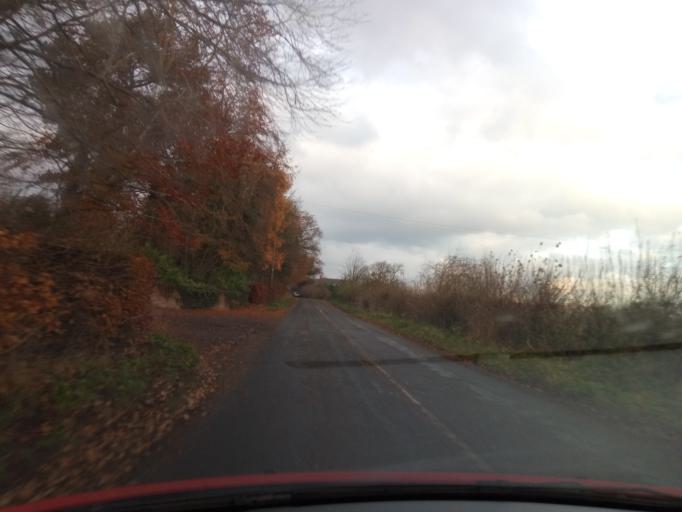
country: GB
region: Scotland
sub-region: The Scottish Borders
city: Newtown St Boswells
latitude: 55.5858
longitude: -2.6812
